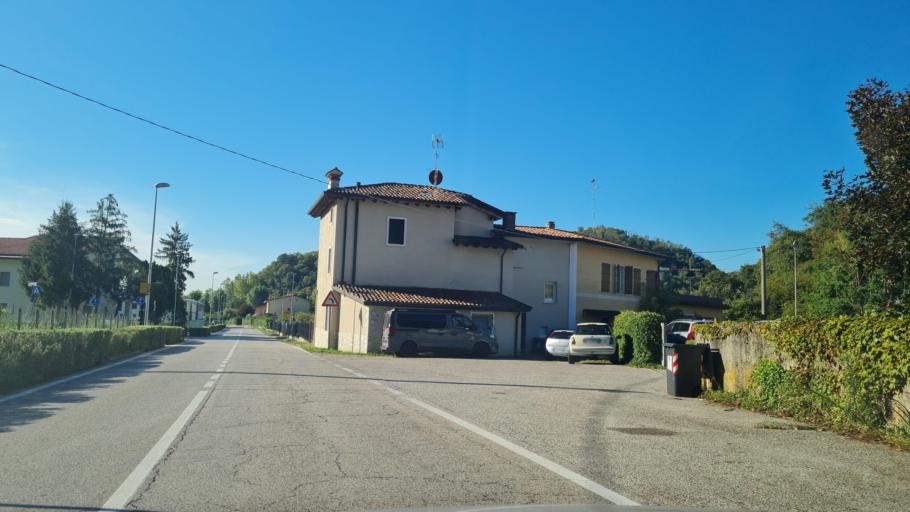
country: IT
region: Veneto
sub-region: Provincia di Vicenza
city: Campese
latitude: 45.7750
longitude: 11.6919
